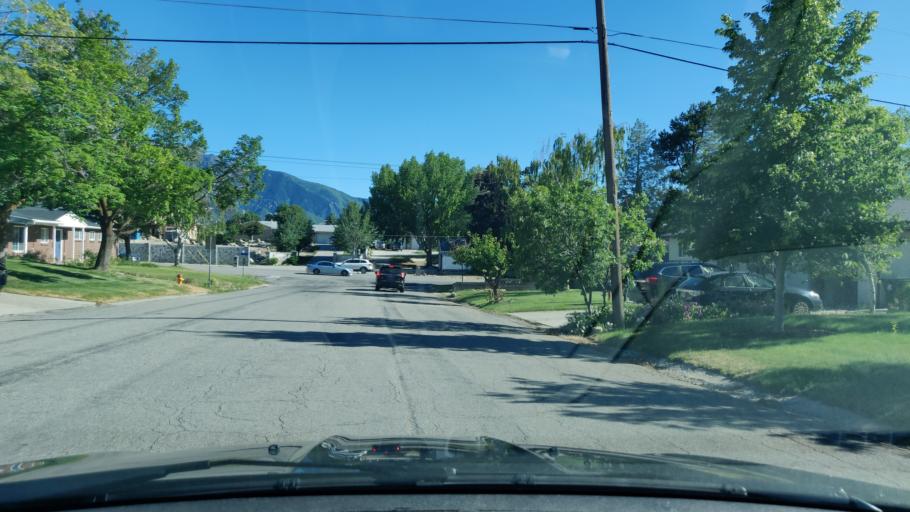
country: US
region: Utah
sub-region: Salt Lake County
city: Cottonwood Heights
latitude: 40.6102
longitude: -111.8147
